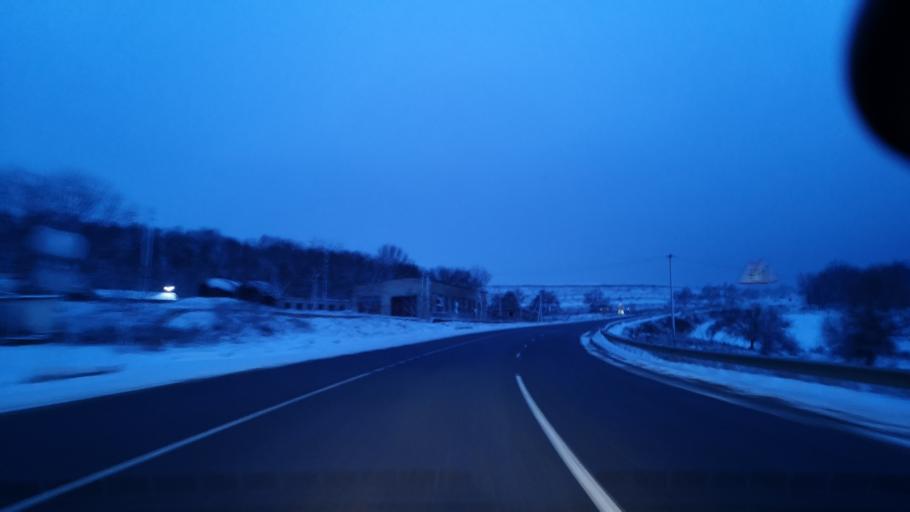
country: MD
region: Rezina
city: Saharna
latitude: 47.5987
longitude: 28.8312
